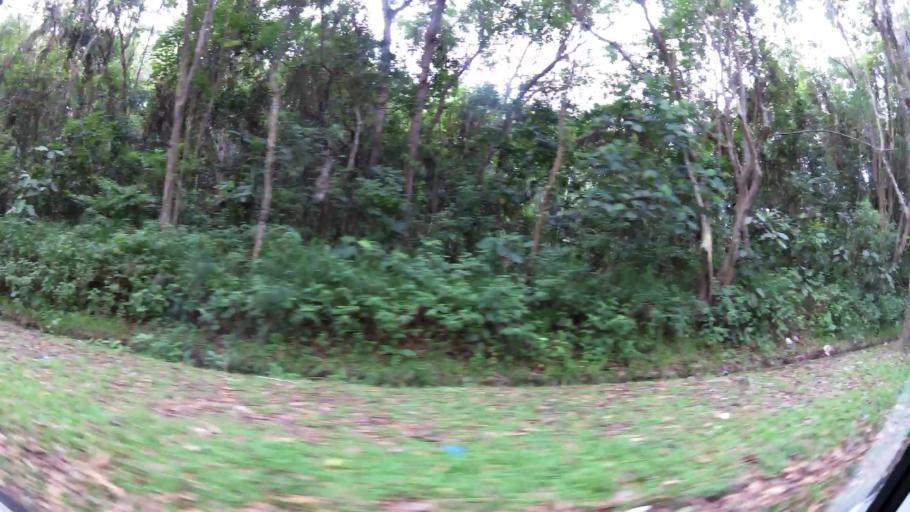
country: BN
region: Brunei and Muara
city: Bandar Seri Begawan
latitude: 4.8750
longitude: 114.8999
